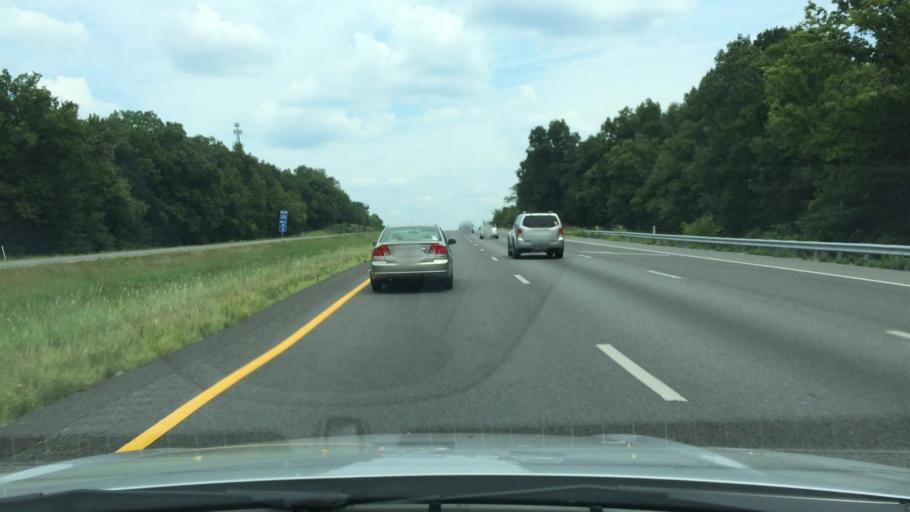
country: US
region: Tennessee
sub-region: Maury County
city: Spring Hill
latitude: 35.6814
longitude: -86.8879
